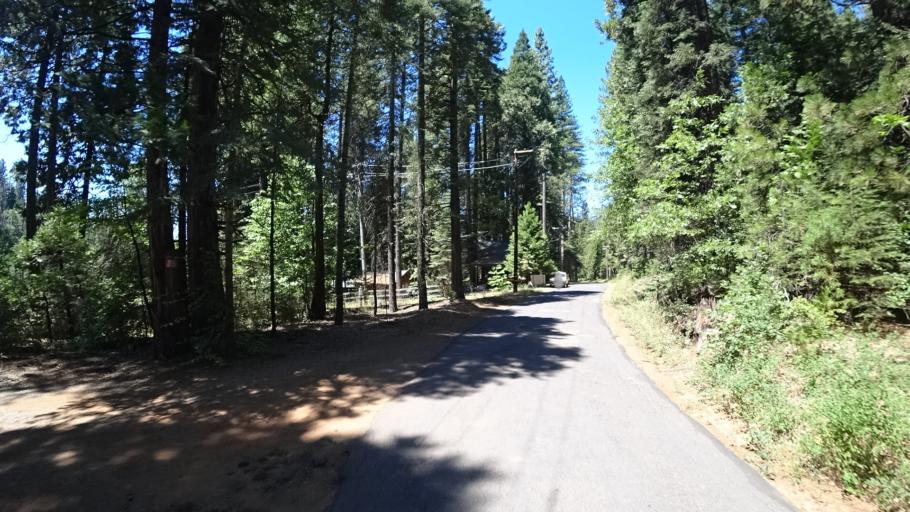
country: US
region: California
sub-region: Calaveras County
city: Arnold
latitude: 38.2373
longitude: -120.3171
